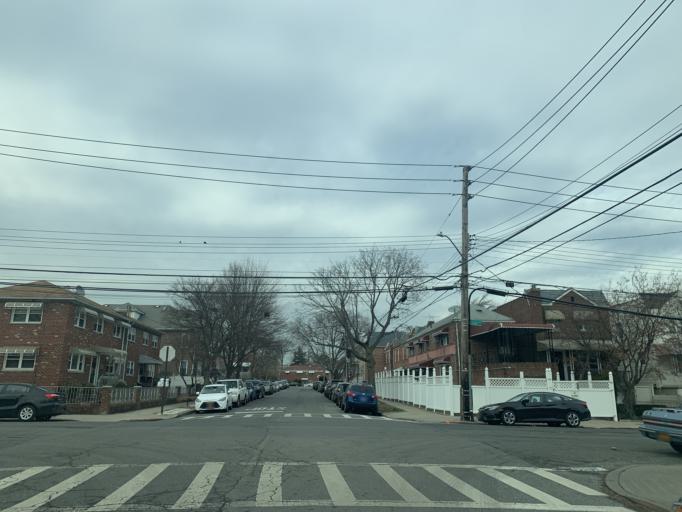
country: US
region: New York
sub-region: Bronx
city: The Bronx
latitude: 40.8596
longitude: -73.8530
